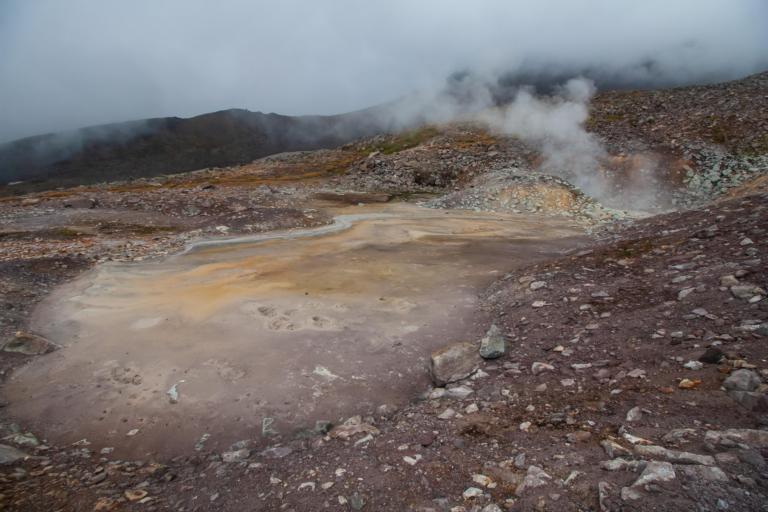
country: RU
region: Kamtsjatka
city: Petropavlovsk-Kamchatsky
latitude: 53.6211
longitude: 158.9401
